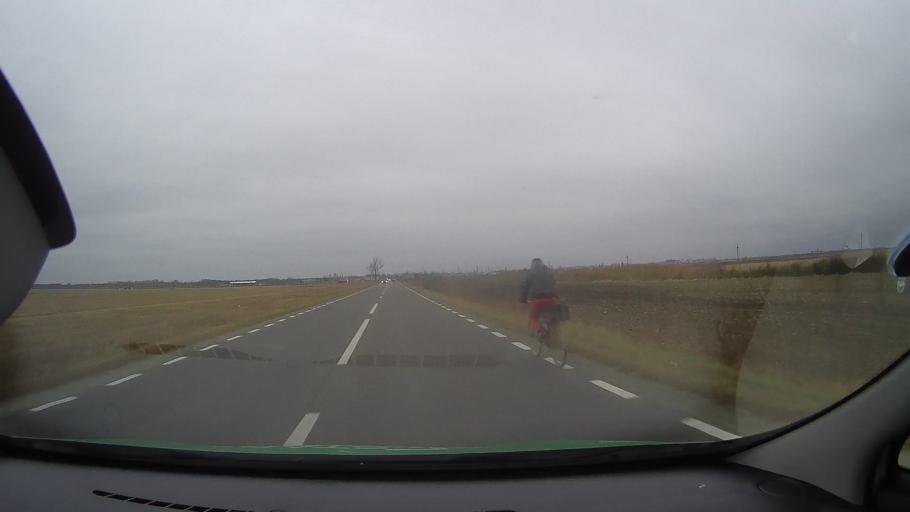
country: RO
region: Ialomita
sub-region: Comuna Slobozia
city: Slobozia
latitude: 44.5887
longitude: 27.3898
